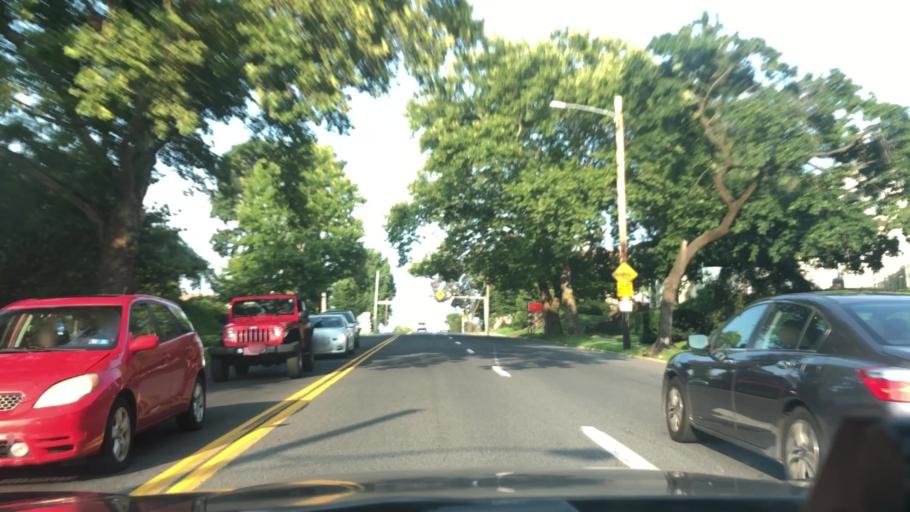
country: US
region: Pennsylvania
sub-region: Lehigh County
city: Allentown
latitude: 40.5955
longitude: -75.4962
